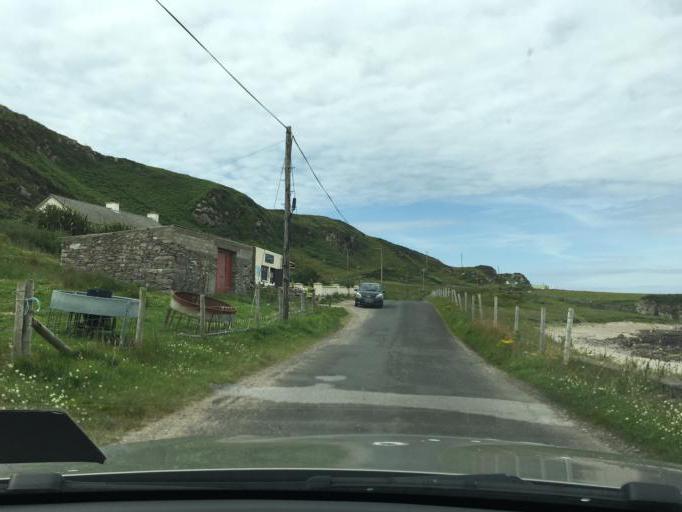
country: IE
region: Ulster
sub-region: County Donegal
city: Carndonagh
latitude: 55.3746
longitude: -7.3484
